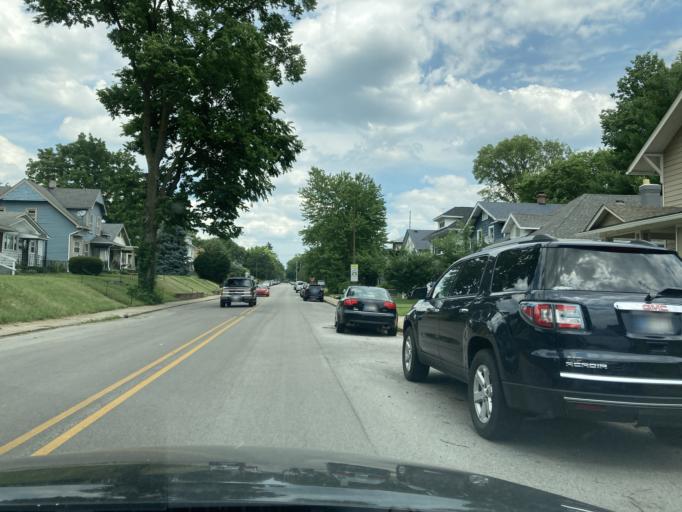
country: US
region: Indiana
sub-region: Marion County
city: Broad Ripple
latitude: 39.8271
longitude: -86.1616
